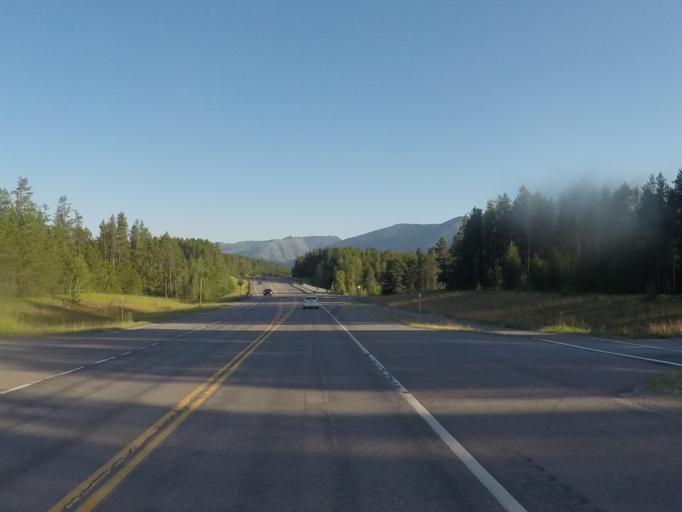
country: US
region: Montana
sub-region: Flathead County
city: Columbia Falls
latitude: 48.4338
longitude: -114.0426
